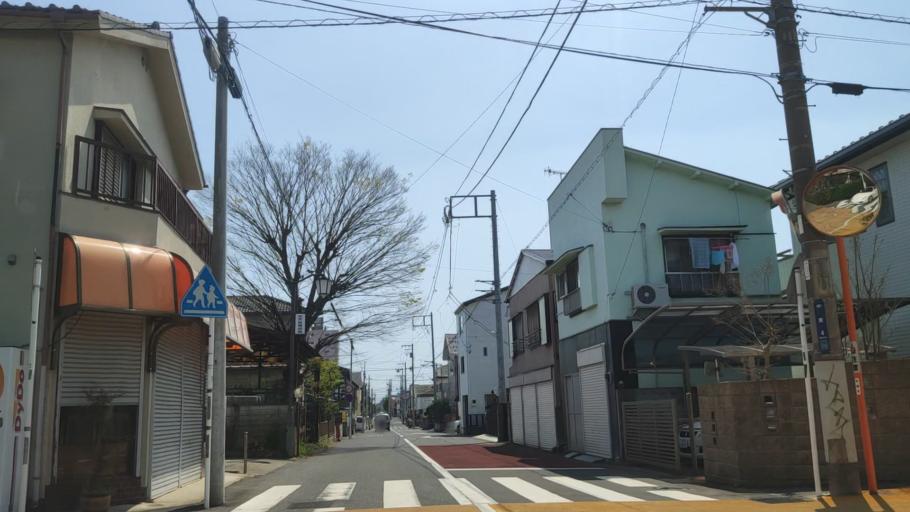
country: JP
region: Kanagawa
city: Hiratsuka
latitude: 35.3334
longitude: 139.3354
